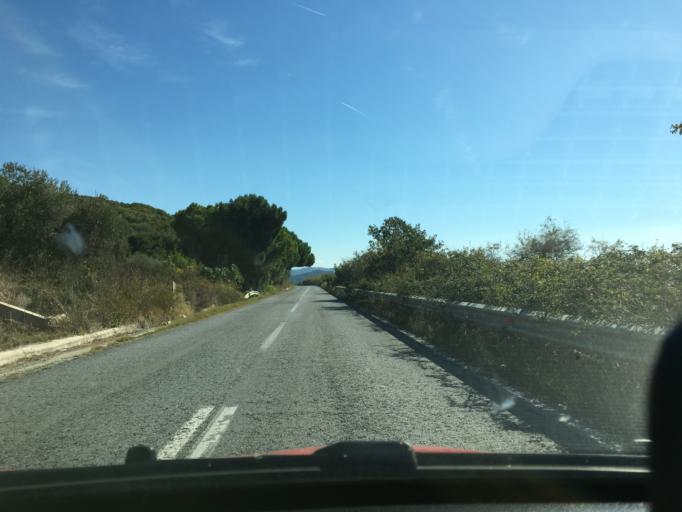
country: GR
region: Central Macedonia
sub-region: Nomos Chalkidikis
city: Nea Roda
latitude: 40.3596
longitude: 23.9351
